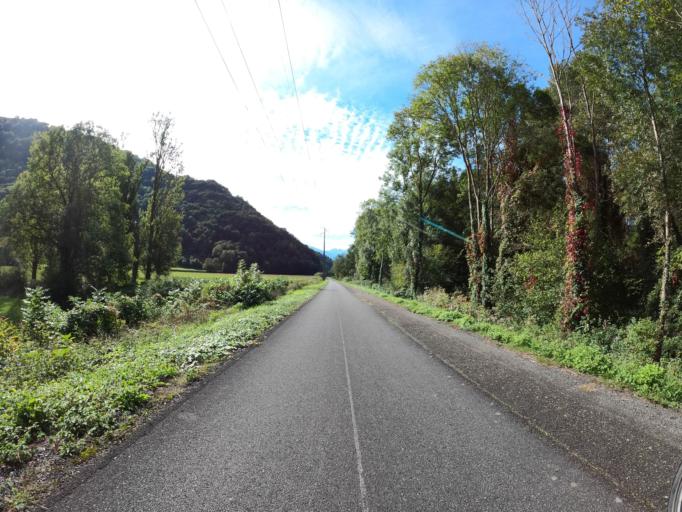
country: FR
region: Midi-Pyrenees
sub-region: Departement des Hautes-Pyrenees
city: Argeles-Gazost
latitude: 43.0390
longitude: -0.0603
